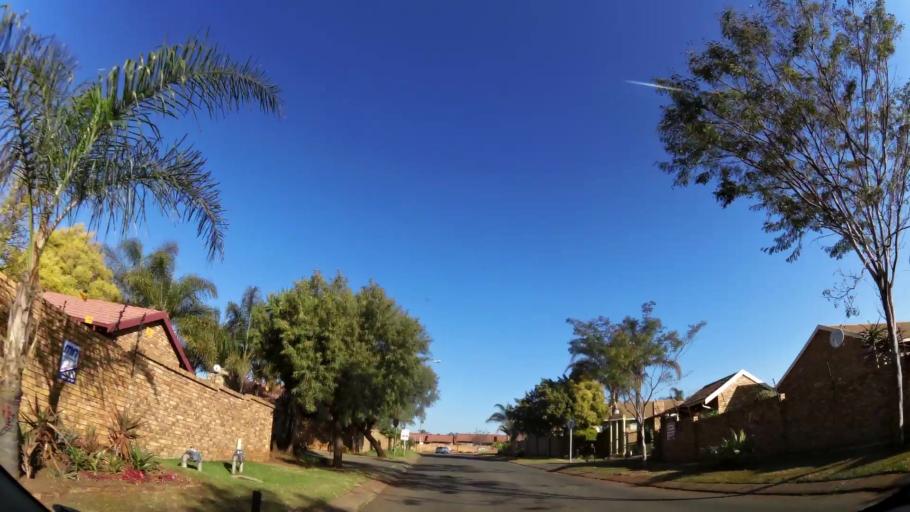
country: ZA
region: Gauteng
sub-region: City of Tshwane Metropolitan Municipality
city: Centurion
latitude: -25.8797
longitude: 28.1423
